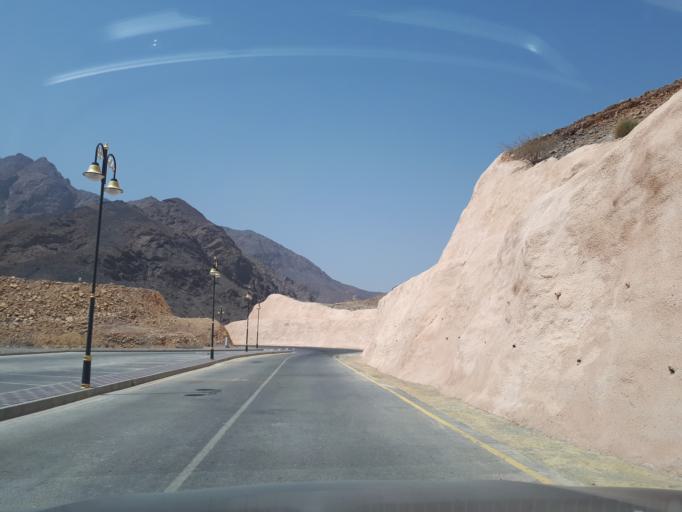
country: OM
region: Ash Sharqiyah
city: Ibra'
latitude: 23.0875
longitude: 58.8483
